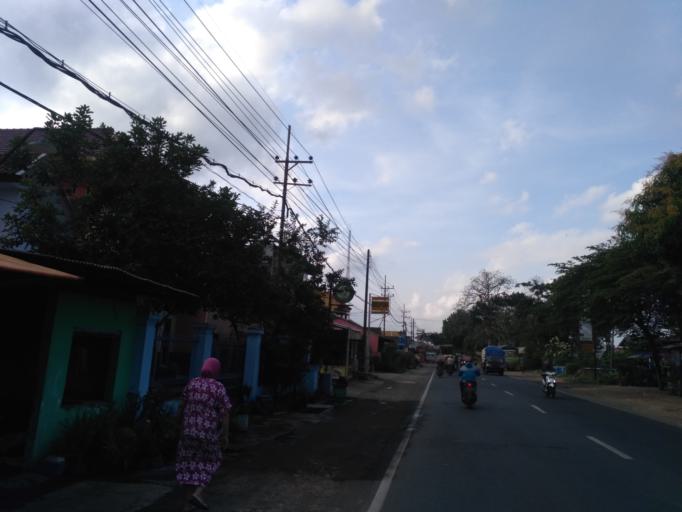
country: ID
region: East Java
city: Wadung
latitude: -8.0473
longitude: 112.6071
